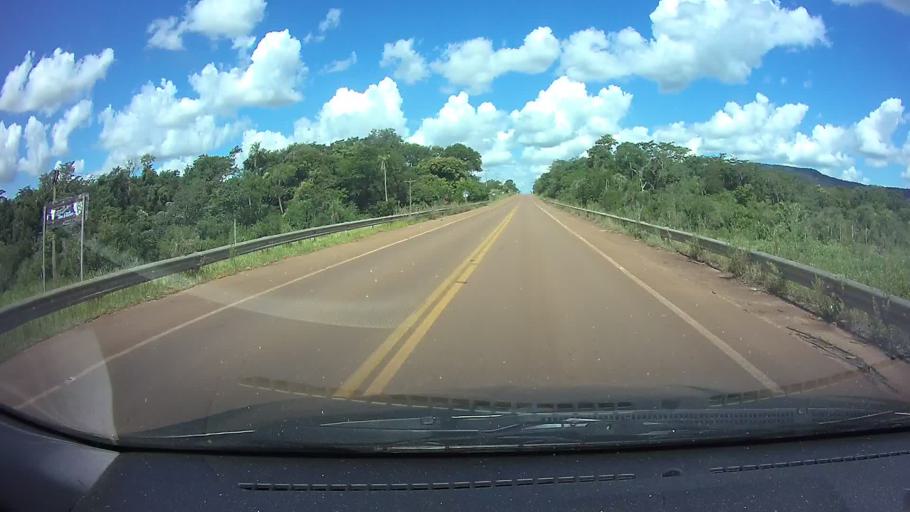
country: PY
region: Paraguari
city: La Colmena
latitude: -25.8989
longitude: -56.7877
